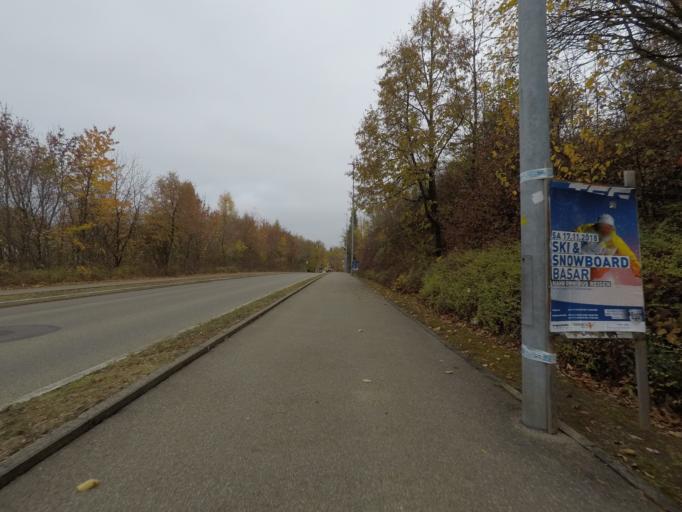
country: DE
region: Baden-Wuerttemberg
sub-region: Tuebingen Region
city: Reutlingen
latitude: 48.5153
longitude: 9.2332
